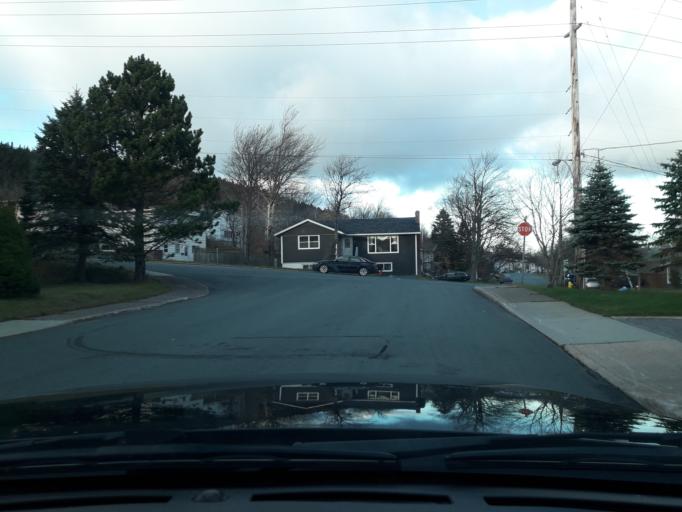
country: CA
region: Newfoundland and Labrador
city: St. John's
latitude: 47.5650
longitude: -52.7524
